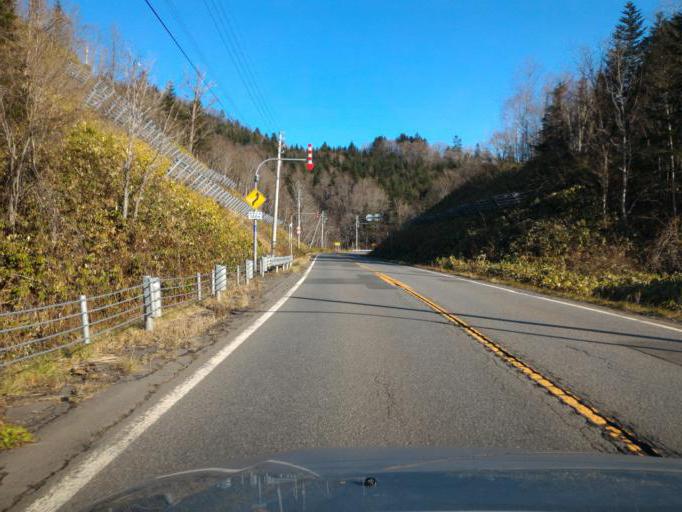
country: JP
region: Hokkaido
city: Bibai
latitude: 43.2779
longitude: 142.0550
